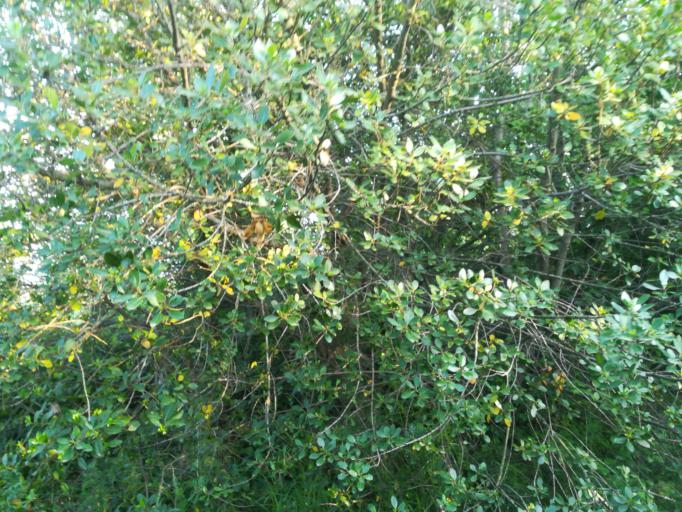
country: IT
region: The Marches
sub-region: Provincia di Macerata
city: Villa Potenza
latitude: 43.2913
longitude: 13.4150
